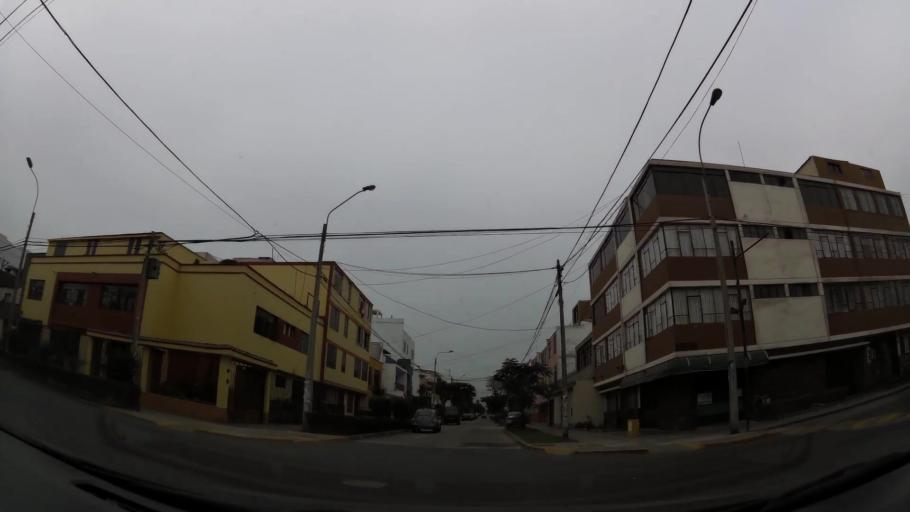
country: PE
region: Lima
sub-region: Lima
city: San Isidro
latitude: -12.0832
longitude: -77.0632
